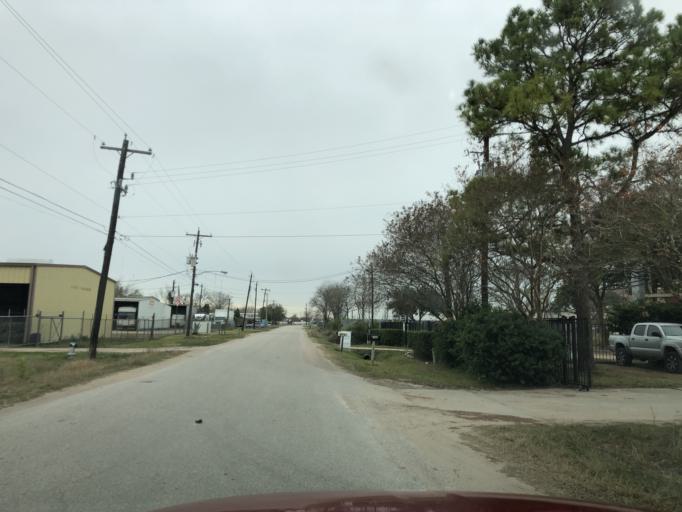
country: US
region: Texas
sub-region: Fort Bend County
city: Missouri City
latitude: 29.6343
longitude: -95.5225
